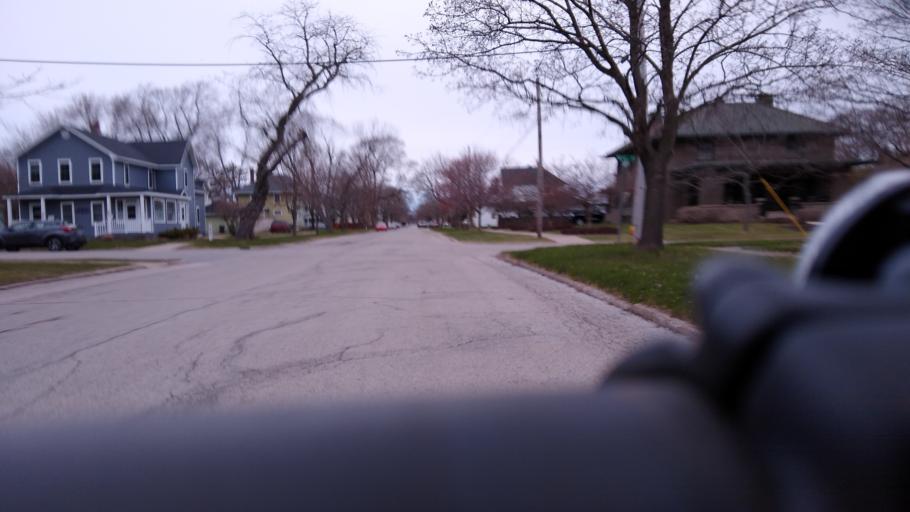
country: US
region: Michigan
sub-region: Delta County
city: Escanaba
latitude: 45.7422
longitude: -87.0548
